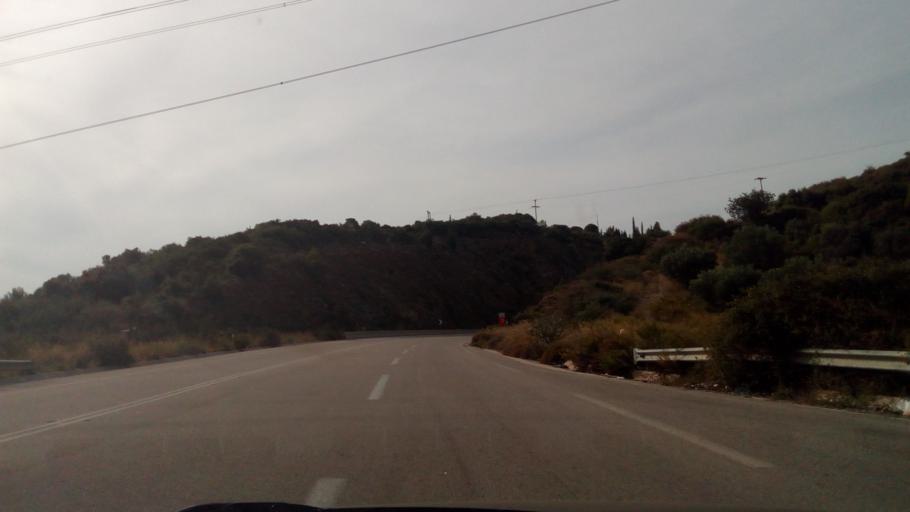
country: GR
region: West Greece
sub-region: Nomos Aitolias kai Akarnanias
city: Nafpaktos
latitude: 38.4030
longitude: 21.8363
